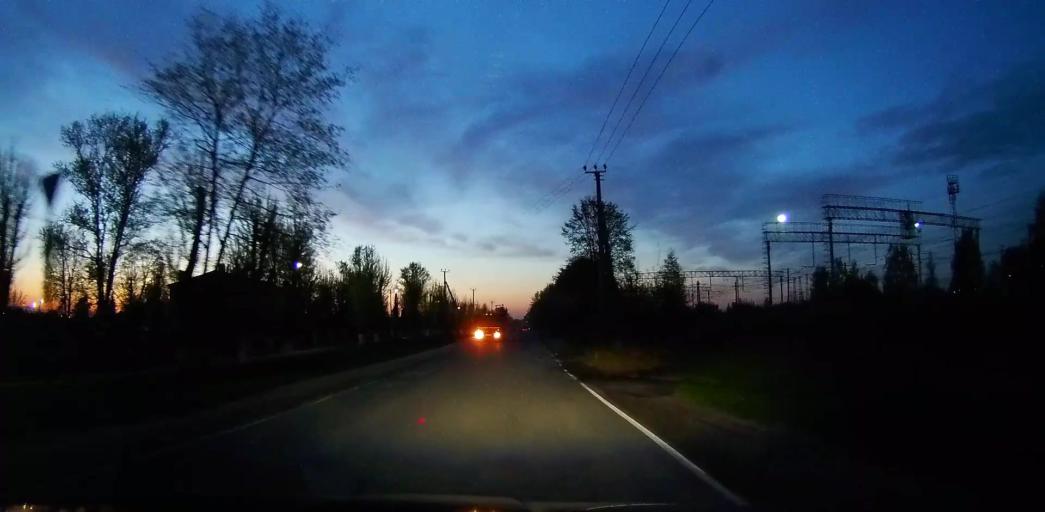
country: RU
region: Moskovskaya
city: Peski
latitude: 55.2106
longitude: 38.7725
